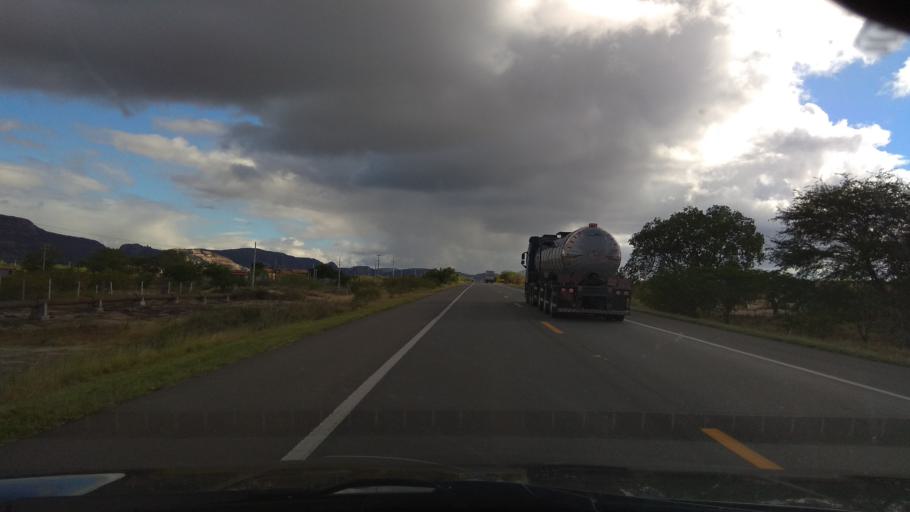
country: BR
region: Bahia
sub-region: Castro Alves
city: Castro Alves
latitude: -12.7004
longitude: -39.7123
